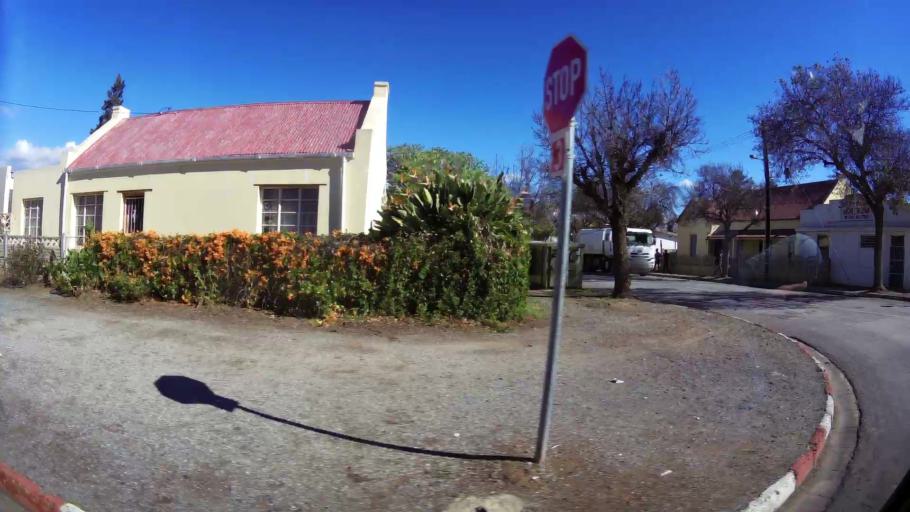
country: ZA
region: Western Cape
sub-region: Cape Winelands District Municipality
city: Ashton
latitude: -33.7967
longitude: 19.8872
